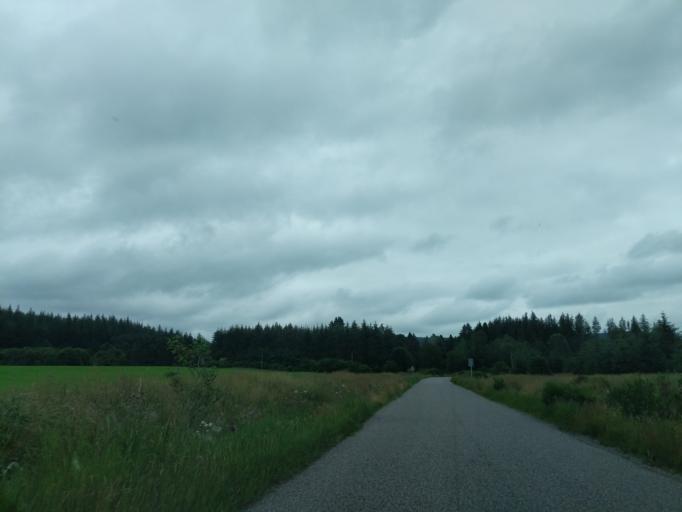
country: GB
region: Scotland
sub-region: Moray
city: Kinloss
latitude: 57.5528
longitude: -3.4929
